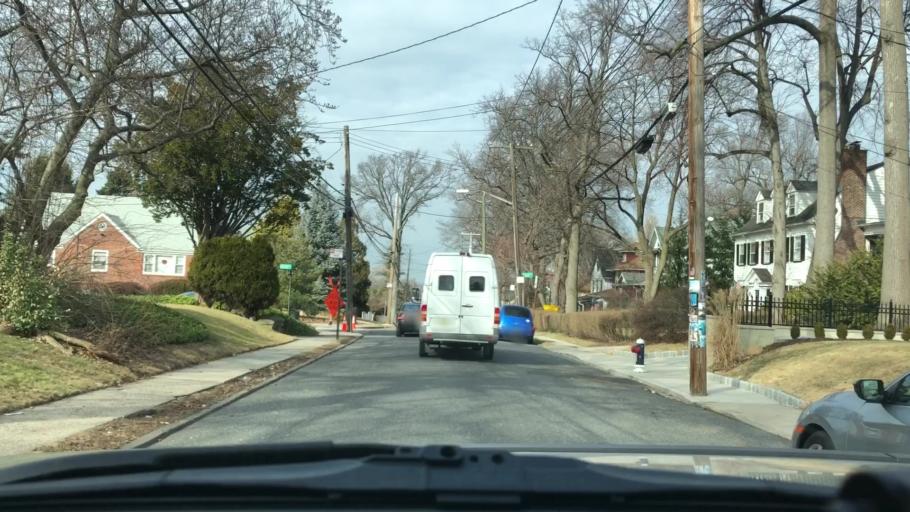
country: US
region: New Jersey
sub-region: Hudson County
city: Bayonne
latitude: 40.6325
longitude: -74.1061
